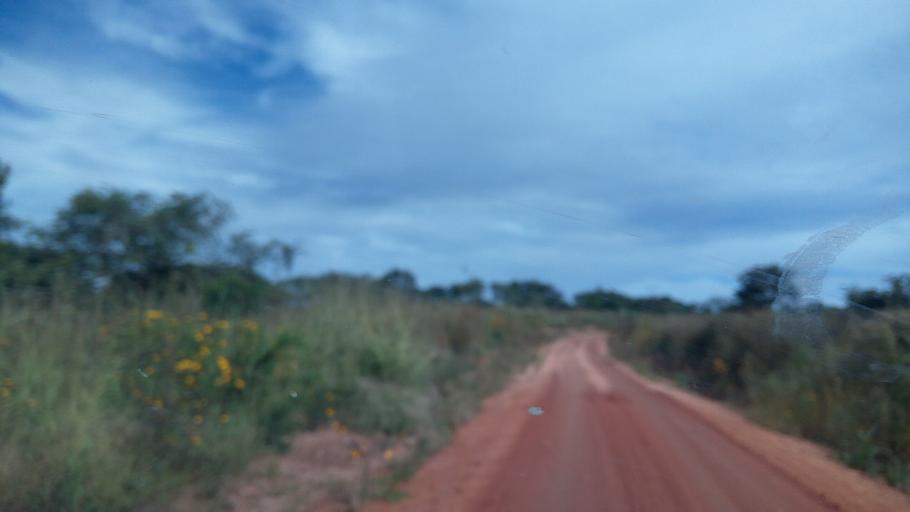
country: CD
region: Katanga
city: Kalemie
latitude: -6.1046
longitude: 28.8903
